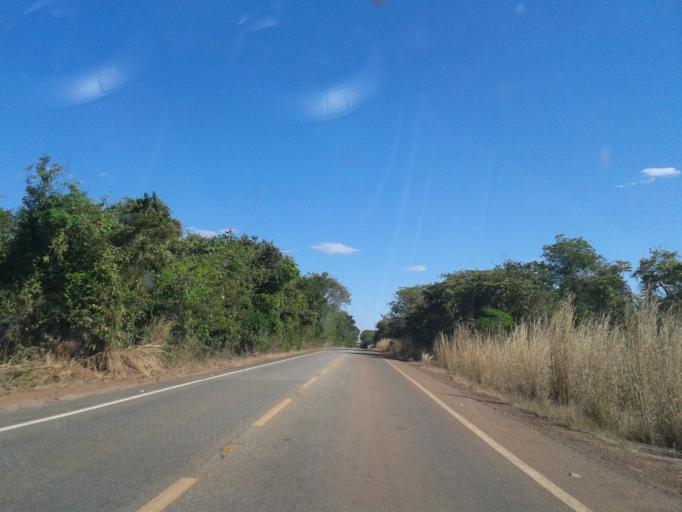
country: BR
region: Goias
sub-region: Mozarlandia
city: Mozarlandia
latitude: -14.4251
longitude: -50.4524
